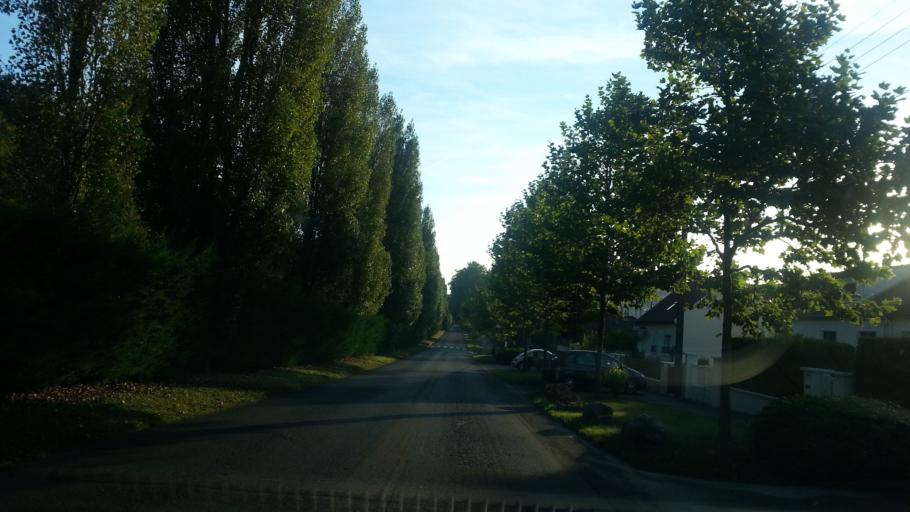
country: FR
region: Picardie
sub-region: Departement de l'Oise
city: Venette
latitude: 49.3989
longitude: 2.8121
